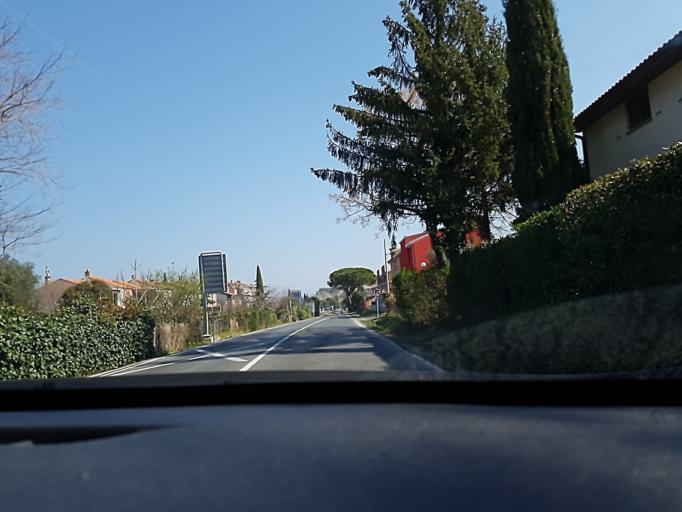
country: SI
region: Izola-Isola
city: Izola
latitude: 45.5347
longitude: 13.6639
